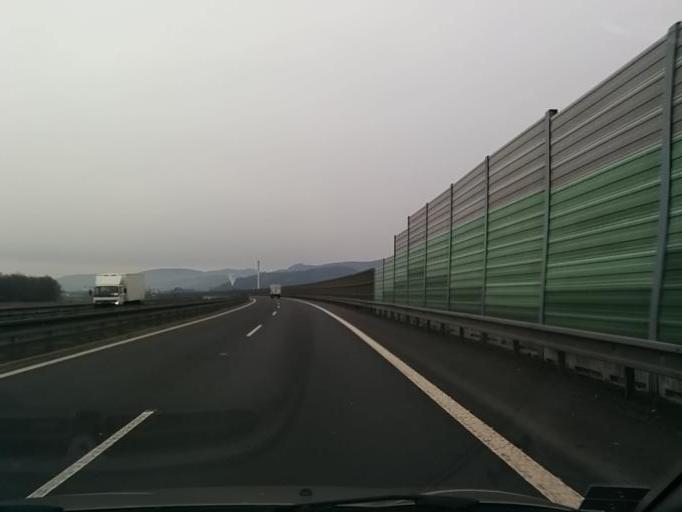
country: SK
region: Banskobystricky
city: Zarnovica
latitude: 48.5343
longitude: 18.7490
